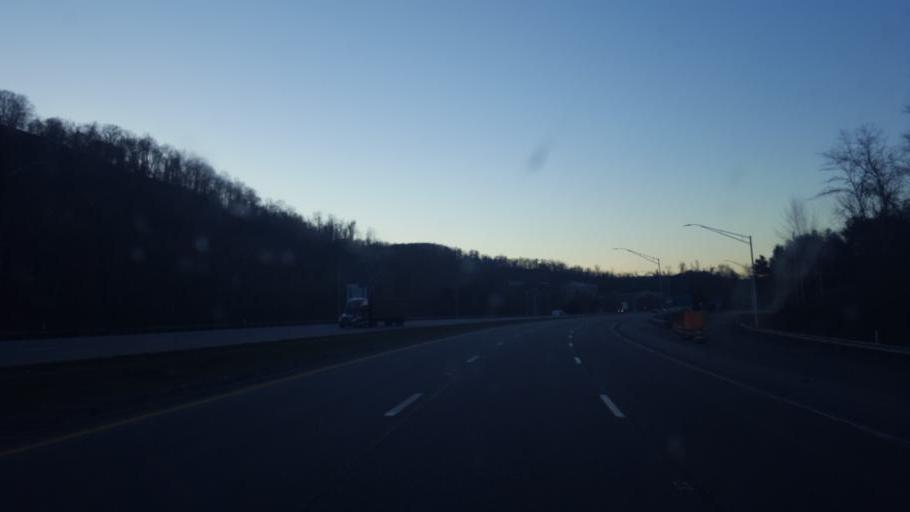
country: US
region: West Virginia
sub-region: Ohio County
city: Bethlehem
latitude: 40.0537
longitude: -80.6760
